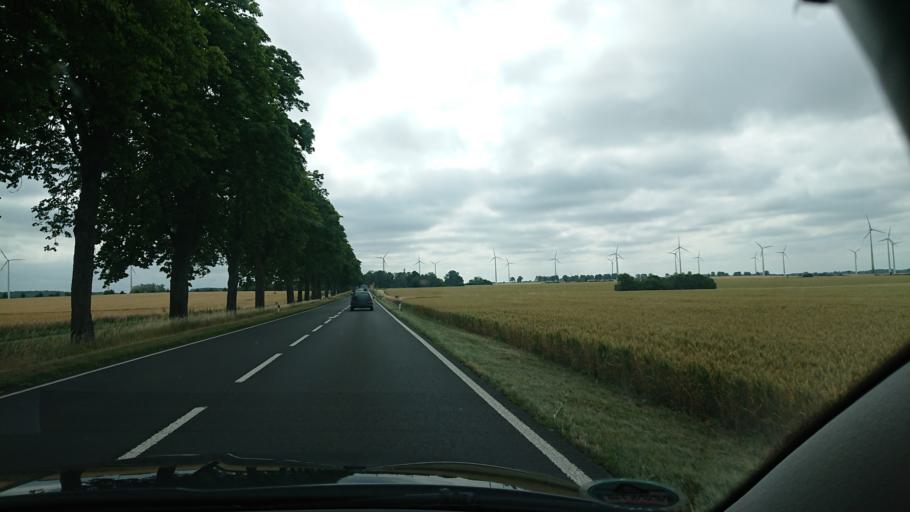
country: DE
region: Brandenburg
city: Plattenburg
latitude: 52.9986
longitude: 12.0766
